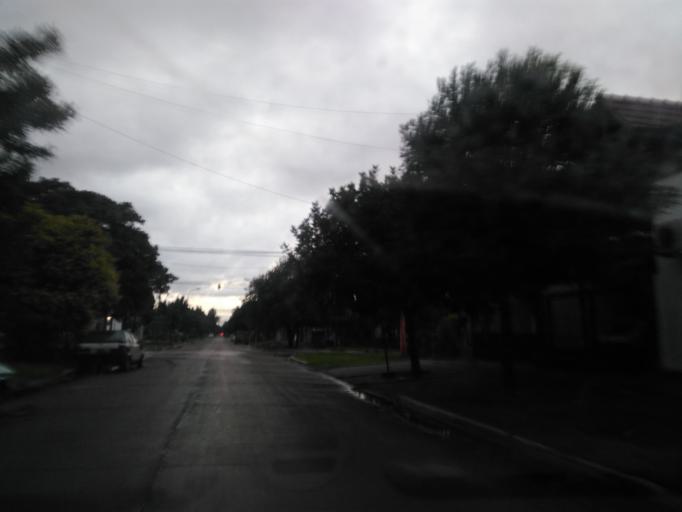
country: AR
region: Chaco
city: Resistencia
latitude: -27.4612
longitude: -58.9942
